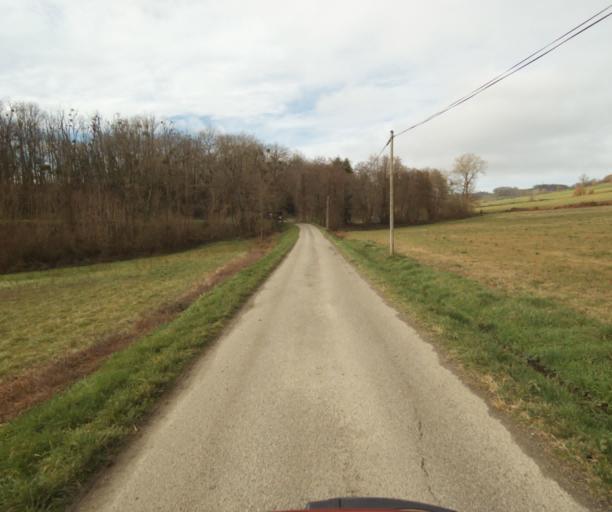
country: FR
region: Midi-Pyrenees
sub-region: Departement de l'Ariege
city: Pamiers
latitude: 43.1017
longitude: 1.5224
